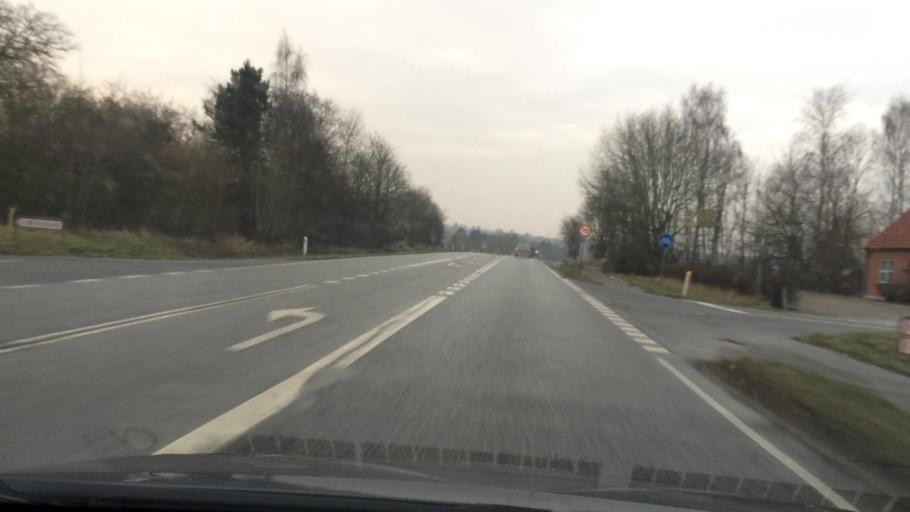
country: DK
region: Central Jutland
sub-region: Horsens Kommune
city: Horsens
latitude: 55.8210
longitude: 9.7909
